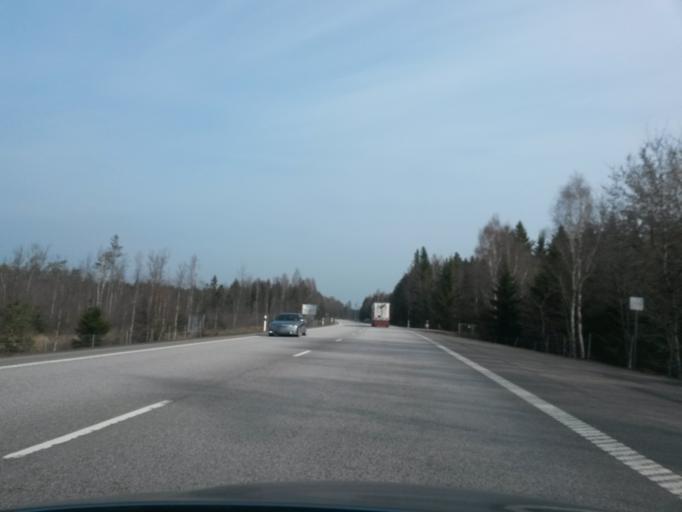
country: SE
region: Vaestra Goetaland
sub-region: Mariestads Kommun
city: Mariestad
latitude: 58.7200
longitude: 13.8827
